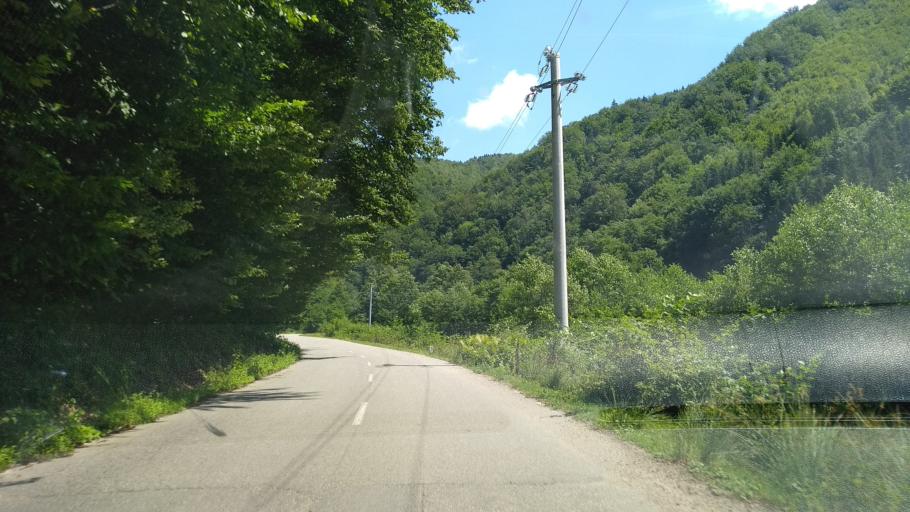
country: RO
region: Hunedoara
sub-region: Comuna Orastioara de Sus
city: Orastioara de Sus
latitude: 45.6213
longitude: 23.2312
